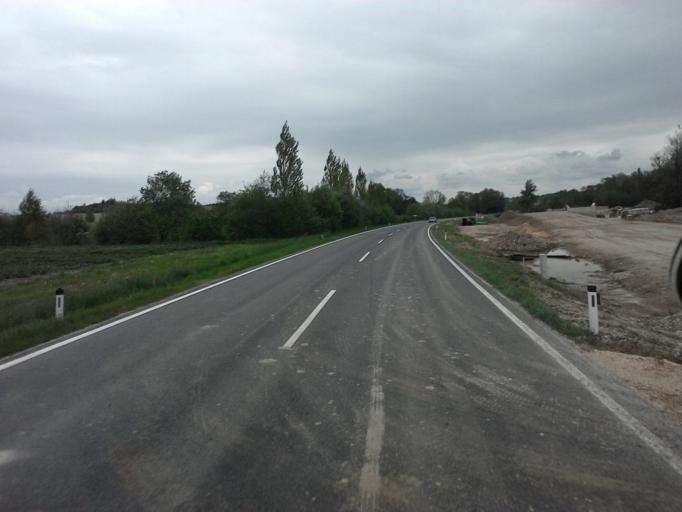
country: AT
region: Upper Austria
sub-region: Politischer Bezirk Vocklabruck
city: Wolfsegg am Hausruck
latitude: 48.2191
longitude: 13.6991
